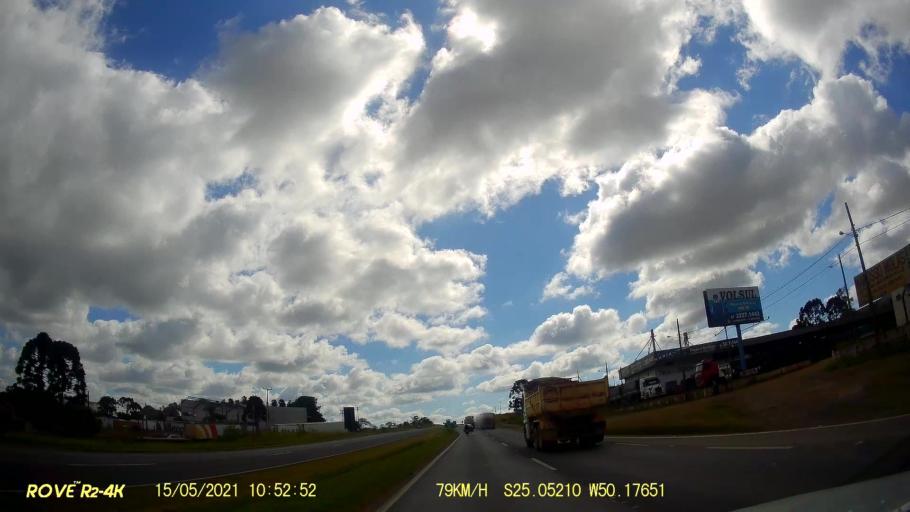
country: BR
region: Parana
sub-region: Ponta Grossa
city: Ponta Grossa
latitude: -25.0523
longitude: -50.1766
